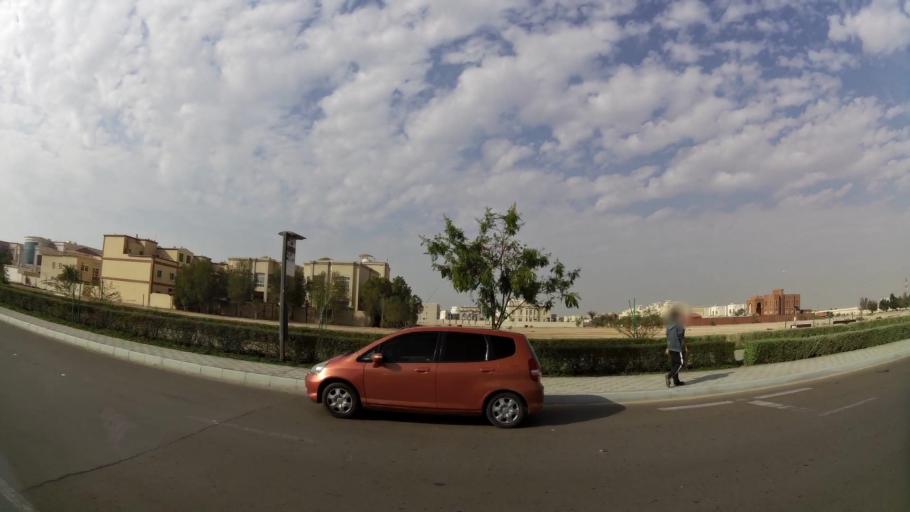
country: AE
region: Abu Dhabi
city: Abu Dhabi
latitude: 24.3484
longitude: 54.5641
